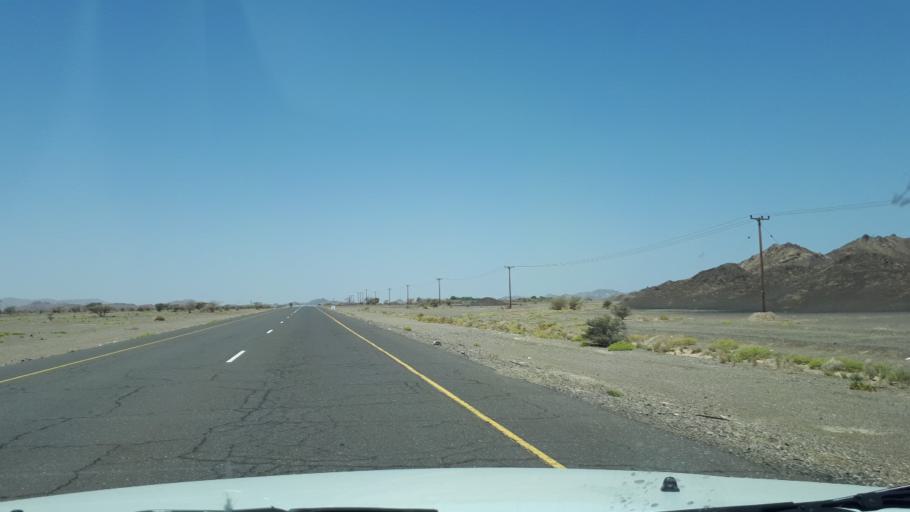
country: OM
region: Ash Sharqiyah
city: Ibra'
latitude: 22.6178
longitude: 58.4345
